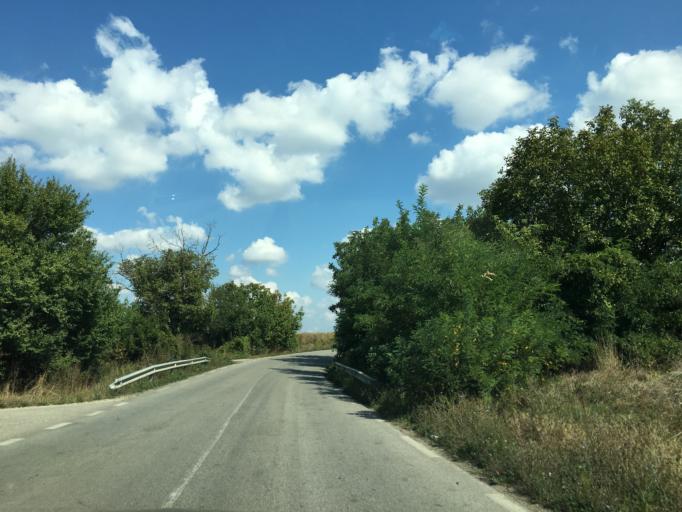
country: BG
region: Montana
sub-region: Obshtina Lom
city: Lom
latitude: 43.8160
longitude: 23.1860
